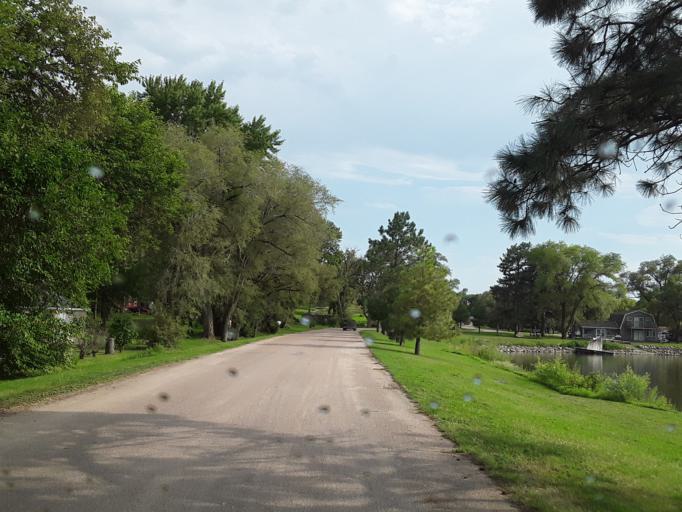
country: US
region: Nebraska
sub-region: Saunders County
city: Ashland
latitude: 41.0999
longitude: -96.4361
